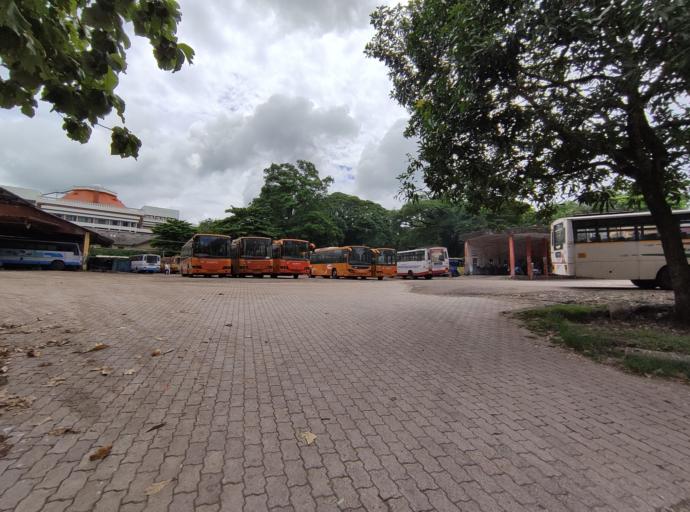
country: IN
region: Kerala
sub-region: Thiruvananthapuram
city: Thiruvananthapuram
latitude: 8.5085
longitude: 76.9467
